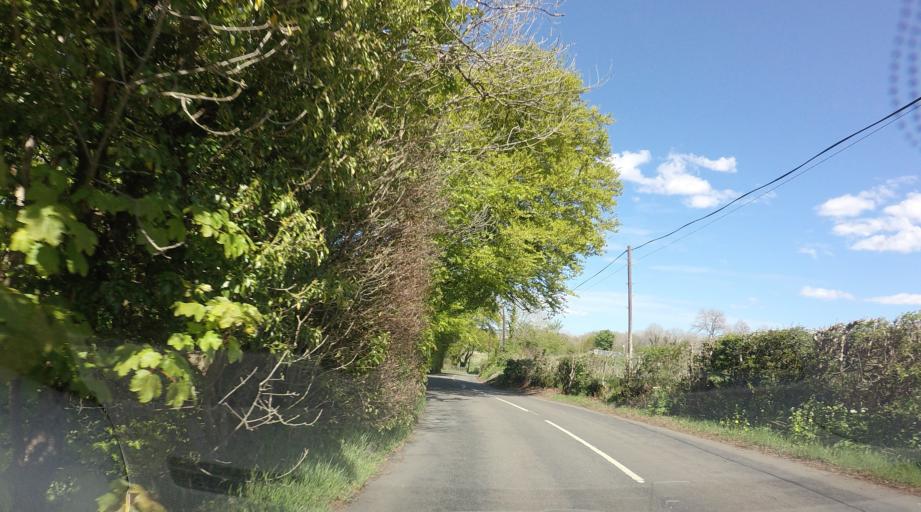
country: GB
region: Scotland
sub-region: Falkirk
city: Polmont
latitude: 55.9682
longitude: -3.6628
